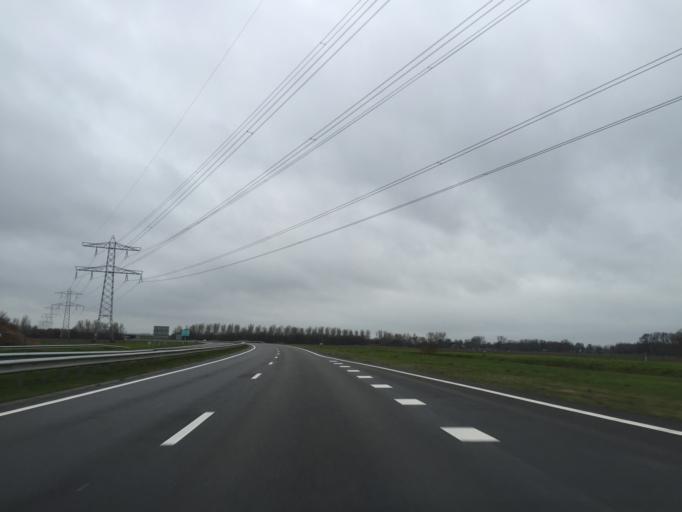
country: NL
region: Zeeland
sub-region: Gemeente Terneuzen
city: Terneuzen
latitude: 51.3222
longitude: 3.7968
